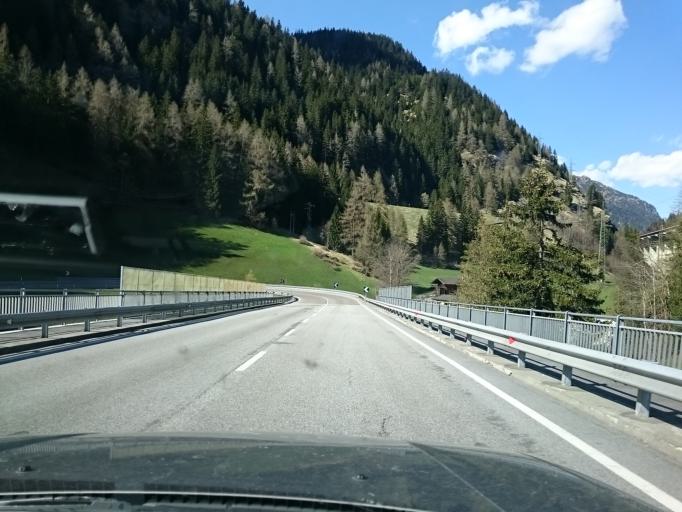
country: IT
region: Trentino-Alto Adige
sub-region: Bolzano
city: Colle Isarco
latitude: 46.9555
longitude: 11.4571
